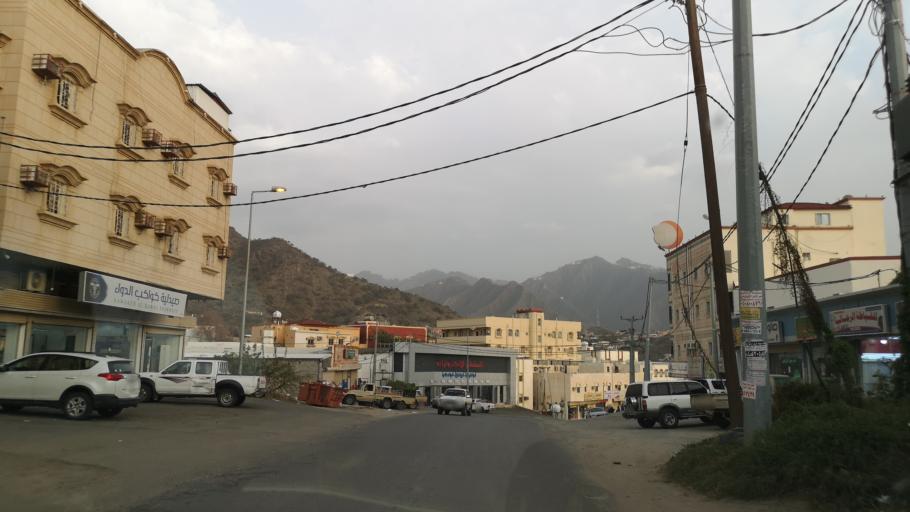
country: YE
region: Sa'dah
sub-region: Monabbih
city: Suq al Khamis
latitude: 17.3546
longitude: 43.1322
